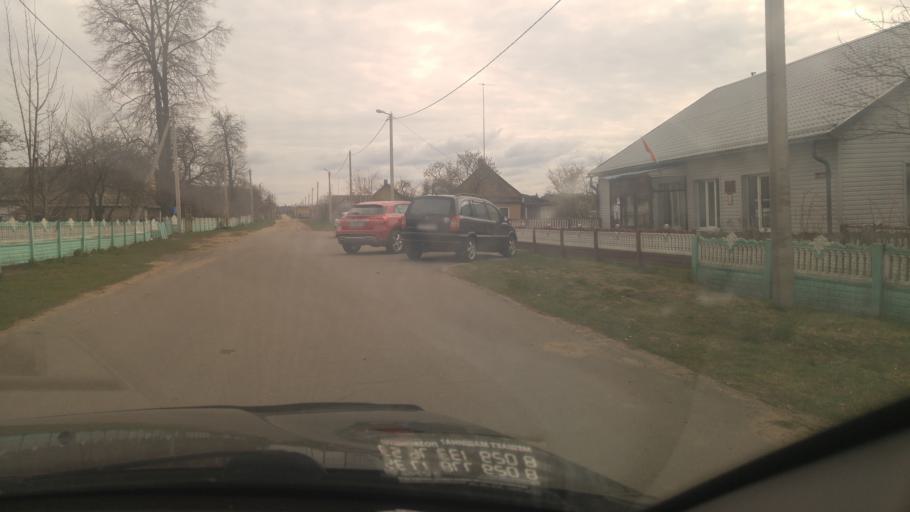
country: BY
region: Minsk
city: Blon'
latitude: 53.5273
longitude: 28.1650
